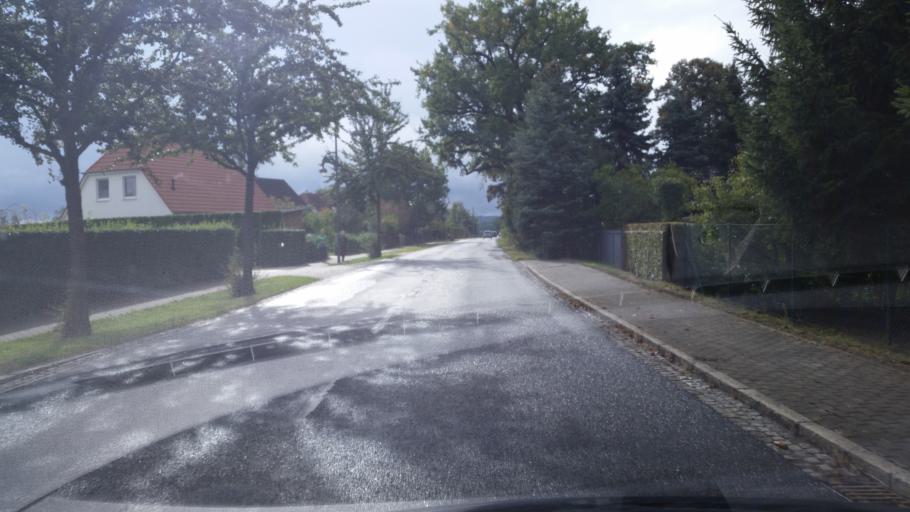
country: DE
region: Saxony
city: Kamenz
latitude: 51.3027
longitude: 14.1264
